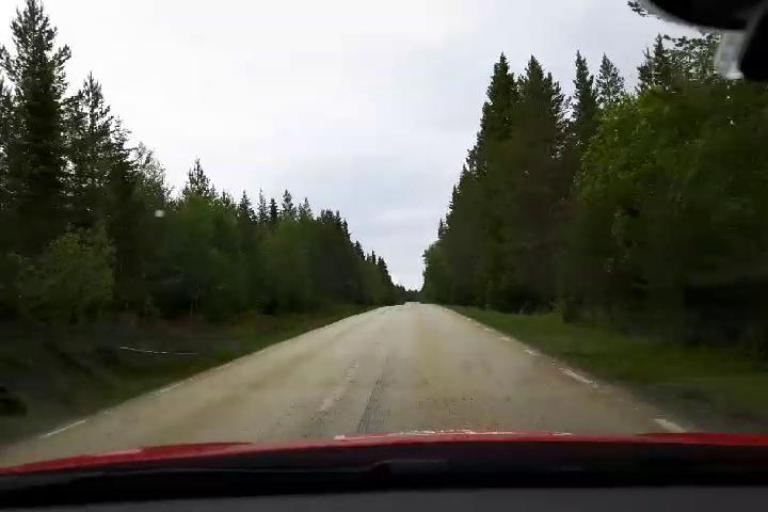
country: SE
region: Jaemtland
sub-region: Bergs Kommun
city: Hoverberg
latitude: 62.8988
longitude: 14.3454
